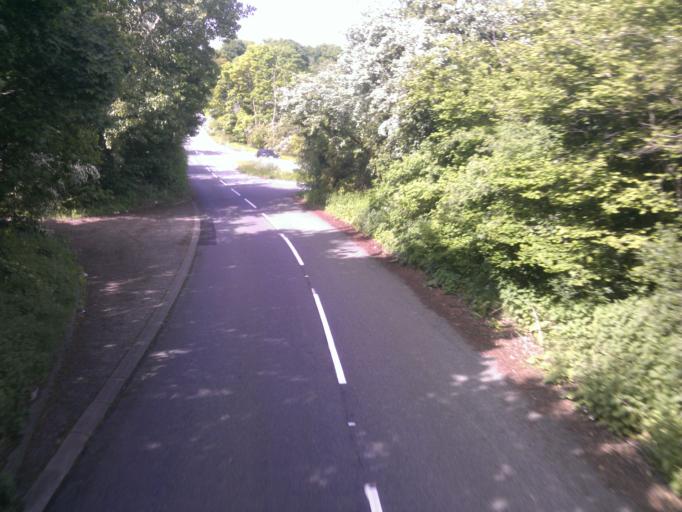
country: GB
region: England
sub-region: Suffolk
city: East Bergholt
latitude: 51.9534
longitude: 0.9619
